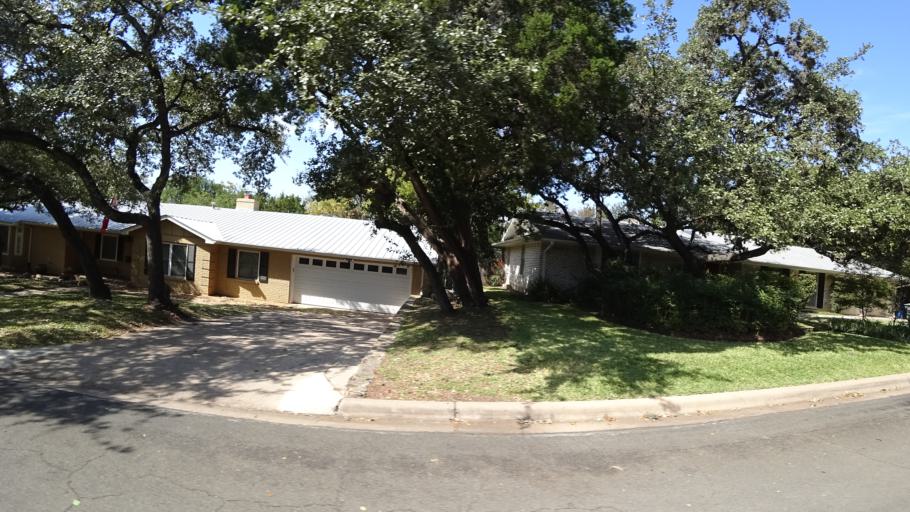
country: US
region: Texas
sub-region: Travis County
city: West Lake Hills
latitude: 30.3461
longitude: -97.7643
